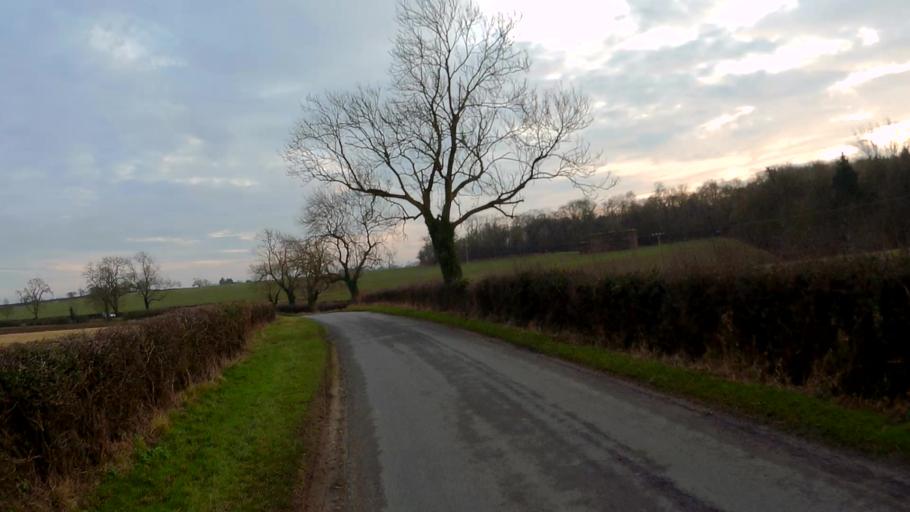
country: GB
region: England
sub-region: Lincolnshire
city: Bourne
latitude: 52.8318
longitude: -0.4463
